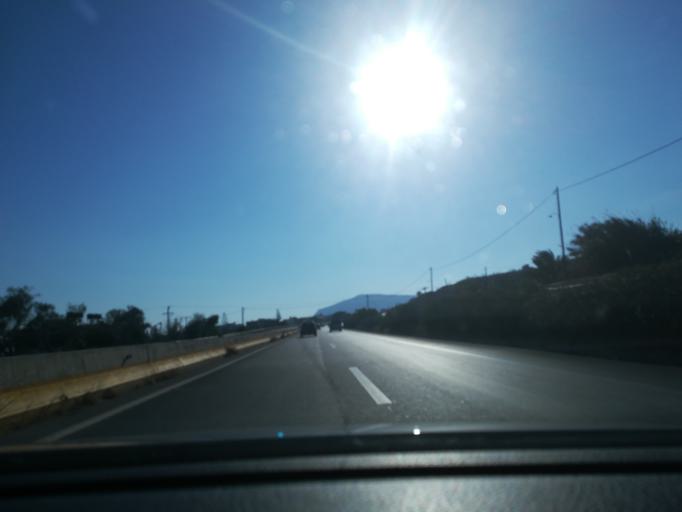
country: GR
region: Crete
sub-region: Nomos Irakleiou
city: Gournes
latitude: 35.3285
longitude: 25.2685
